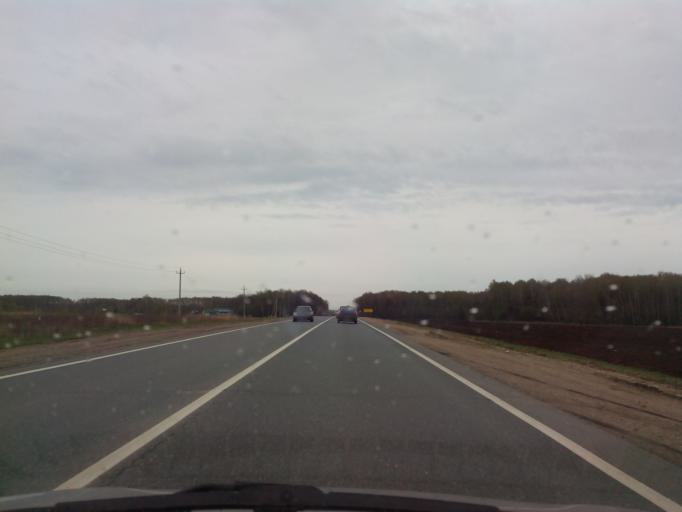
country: RU
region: Moskovskaya
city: Kashira
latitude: 54.7740
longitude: 38.1558
